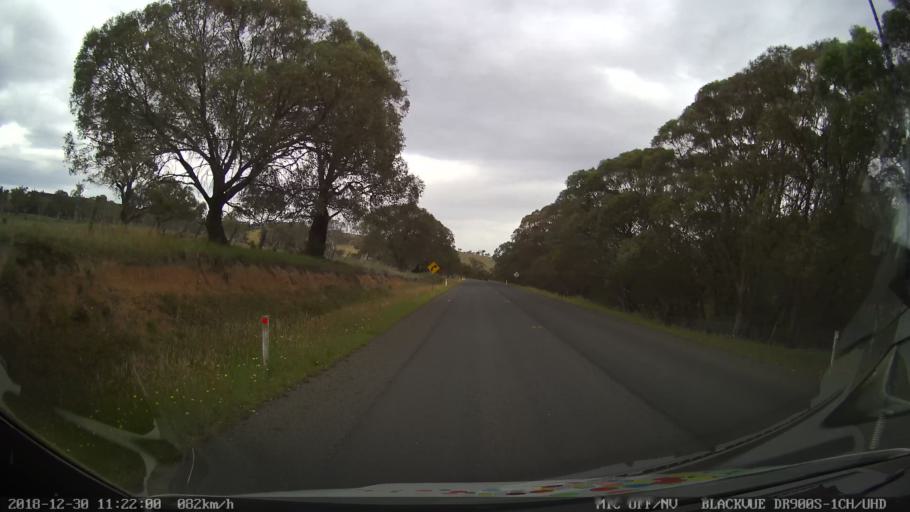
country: AU
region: New South Wales
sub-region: Snowy River
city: Jindabyne
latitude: -36.5050
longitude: 148.6717
